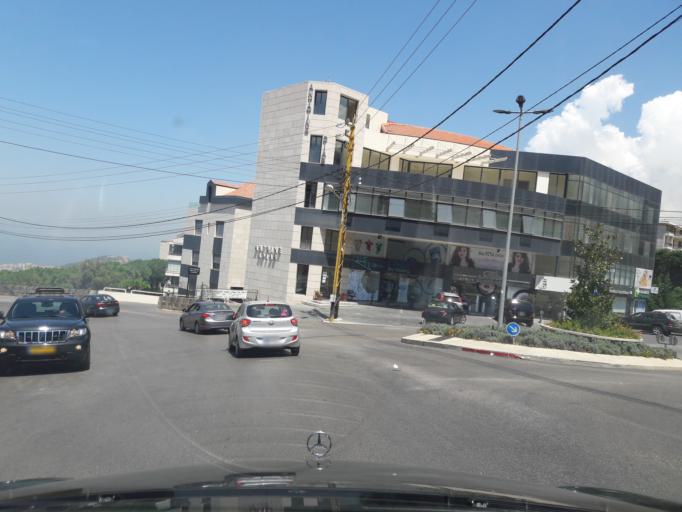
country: LB
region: Mont-Liban
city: Djounie
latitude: 33.9263
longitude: 35.6370
